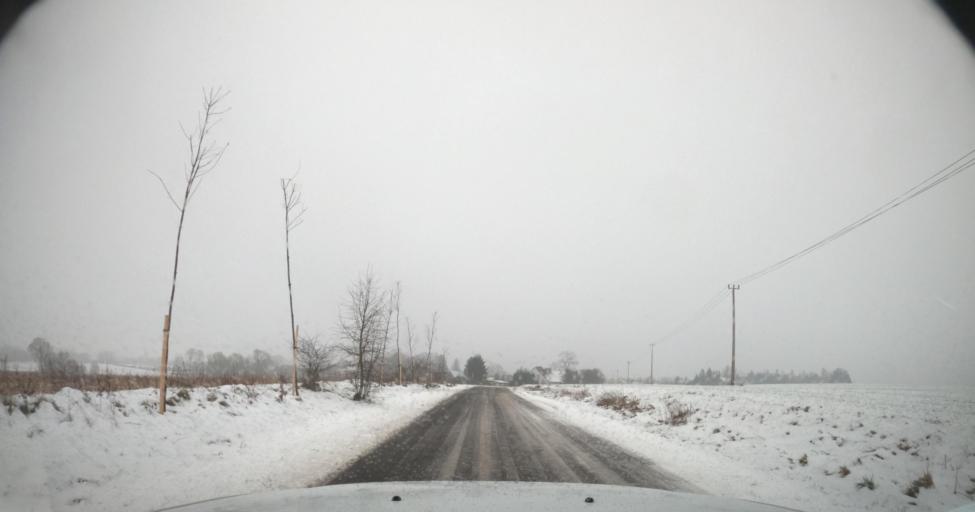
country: PL
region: West Pomeranian Voivodeship
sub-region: Powiat kamienski
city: Golczewo
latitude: 53.7911
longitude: 14.9511
